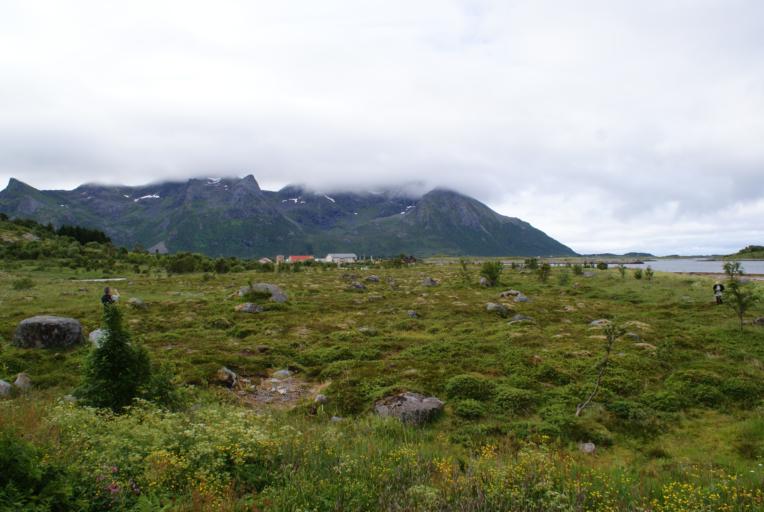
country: NO
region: Nordland
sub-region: Vagan
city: Kabelvag
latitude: 68.2606
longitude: 14.2686
